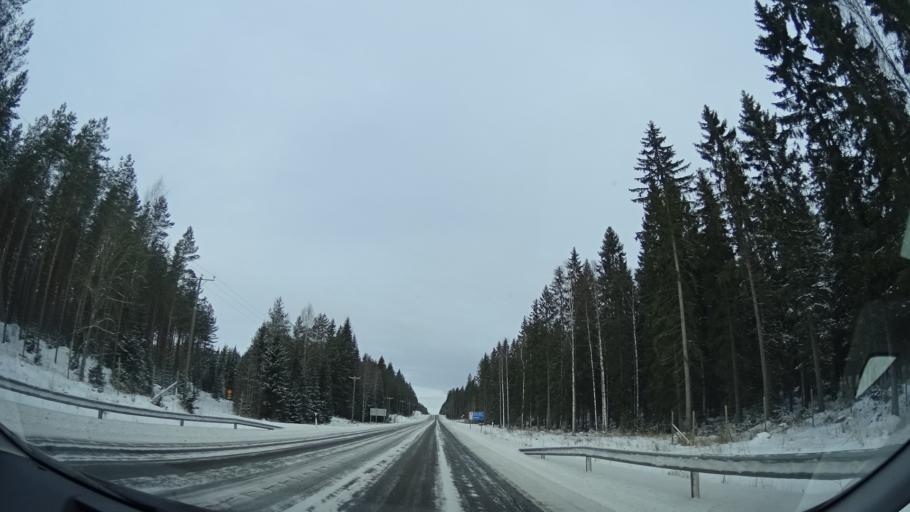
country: FI
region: Uusimaa
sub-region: Helsinki
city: Kaerkoelae
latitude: 60.6512
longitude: 23.8635
